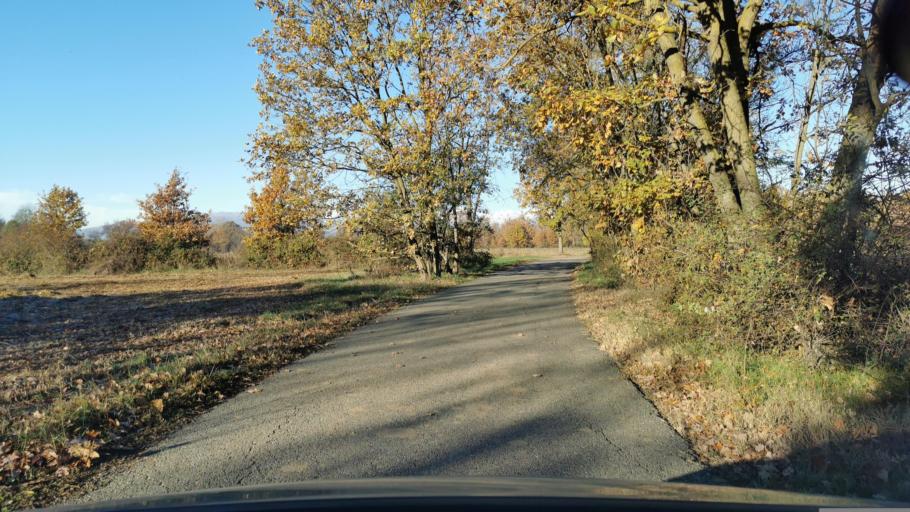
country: IT
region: Piedmont
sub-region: Provincia di Torino
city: Volpiano
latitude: 45.2061
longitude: 7.7639
